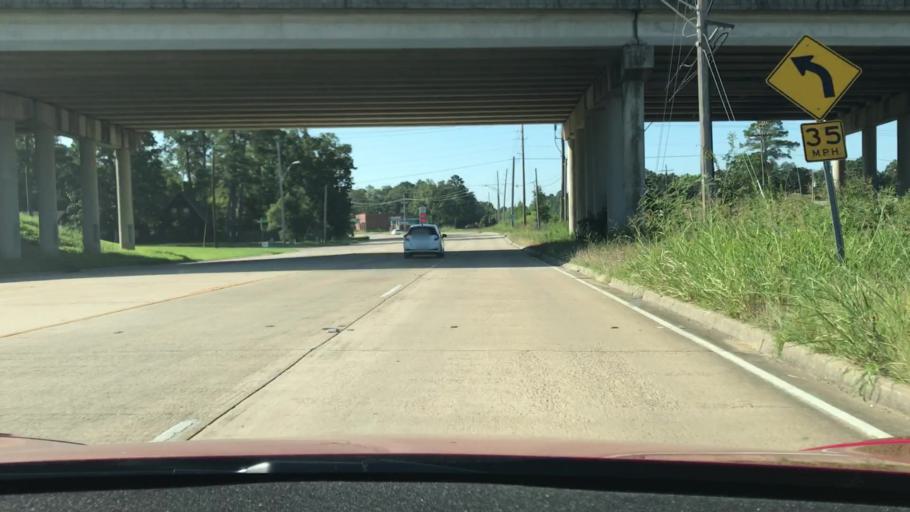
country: US
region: Louisiana
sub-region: Bossier Parish
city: Bossier City
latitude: 32.4014
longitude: -93.7359
